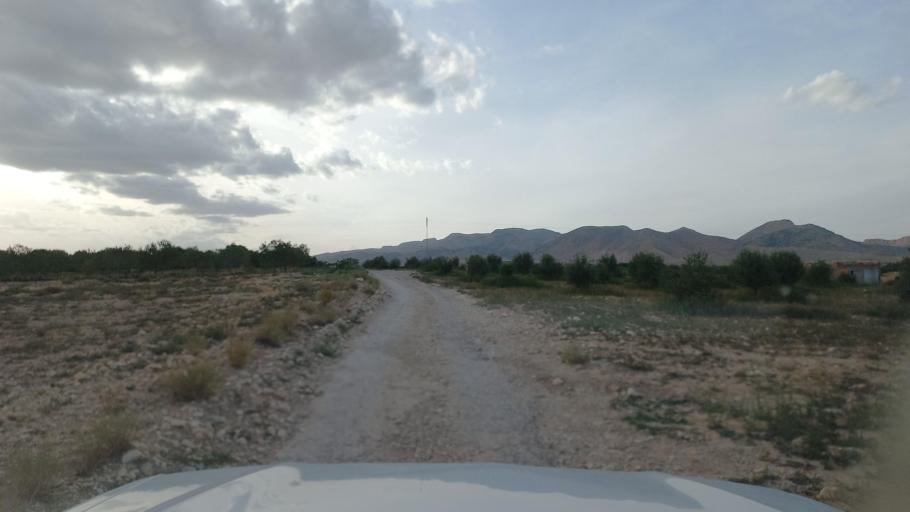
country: TN
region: Al Qasrayn
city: Sbiba
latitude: 35.4360
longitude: 9.0975
